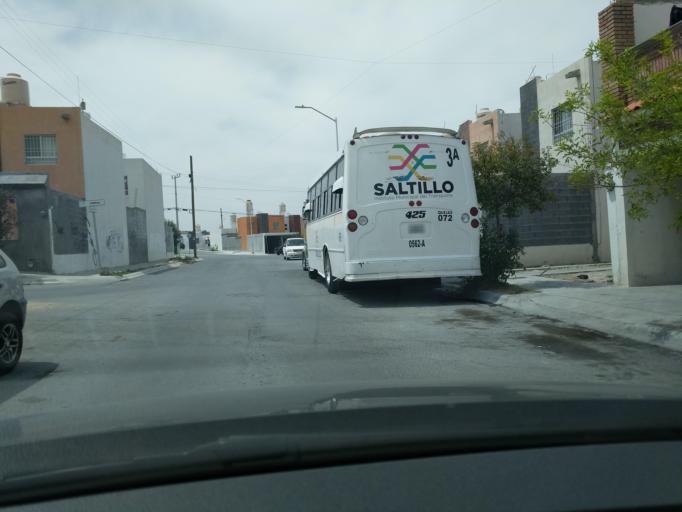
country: MX
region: Coahuila
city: Saltillo
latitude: 25.3469
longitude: -101.0082
